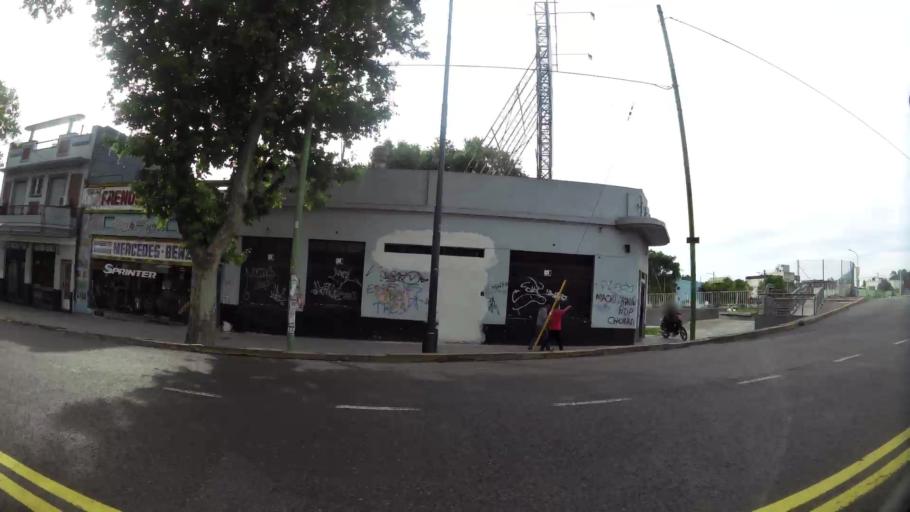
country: AR
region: Buenos Aires F.D.
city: Villa Lugano
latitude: -34.6499
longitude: -58.4700
